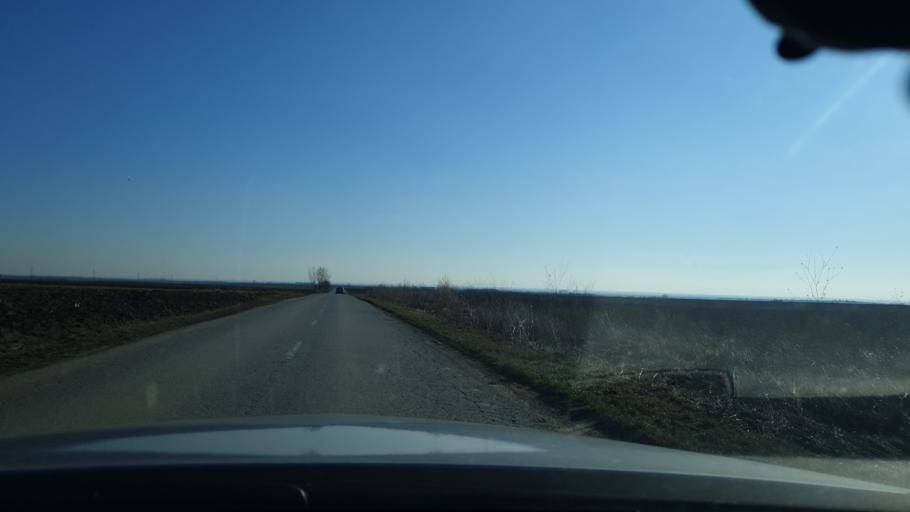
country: RS
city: Vrdnik
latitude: 45.0818
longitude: 19.8076
